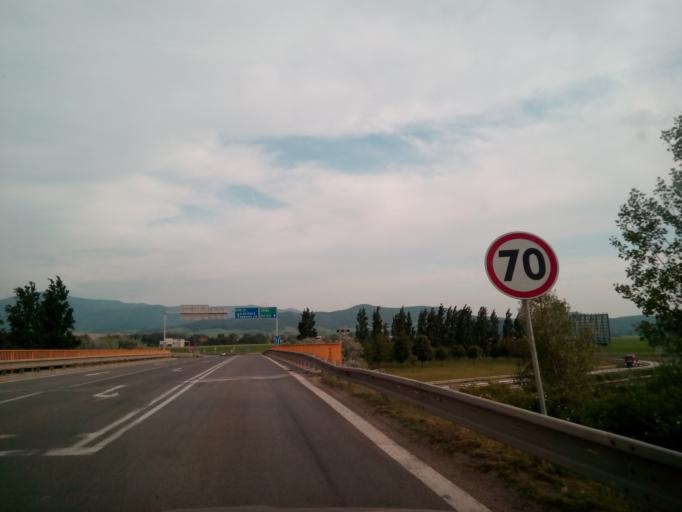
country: SK
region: Trenciansky
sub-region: Okres Trencin
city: Trencin
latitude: 48.8608
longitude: 17.9575
